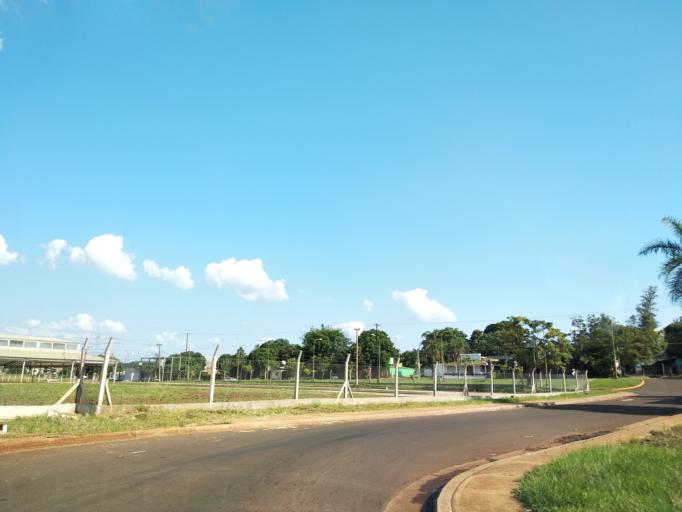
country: AR
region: Misiones
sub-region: Departamento de Capital
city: Posadas
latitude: -27.4136
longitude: -55.8996
